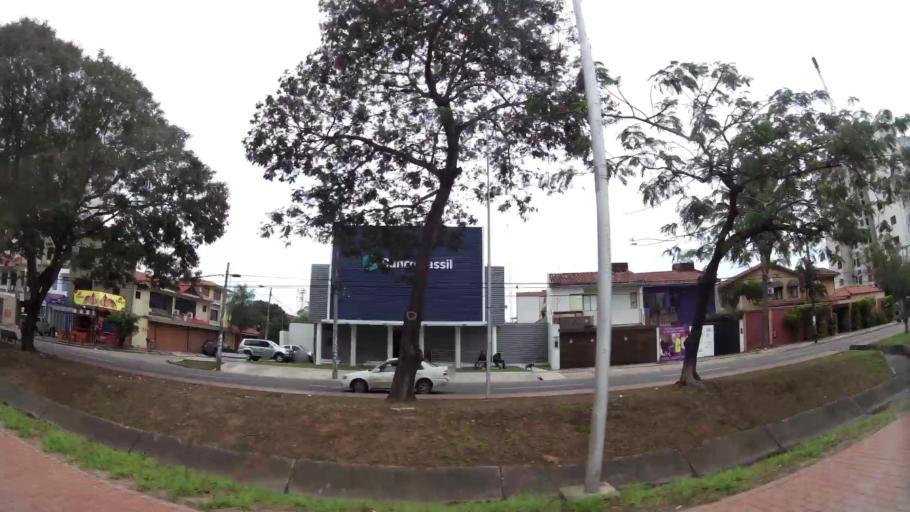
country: BO
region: Santa Cruz
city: Santa Cruz de la Sierra
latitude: -17.7644
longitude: -63.1690
